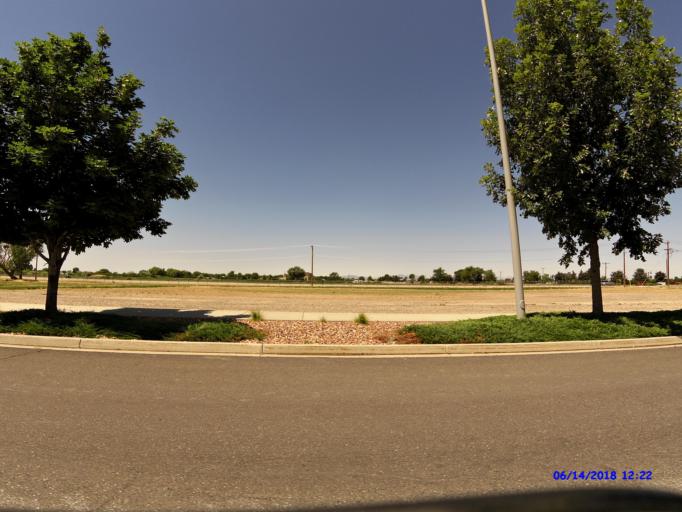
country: US
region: Utah
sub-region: Weber County
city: Marriott-Slaterville
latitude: 41.2661
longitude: -112.0077
